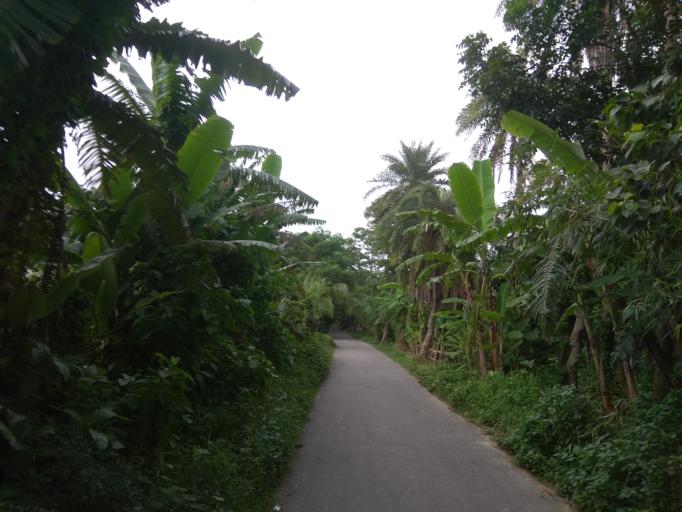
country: BD
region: Dhaka
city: Dohar
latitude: 23.4882
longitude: 89.9966
